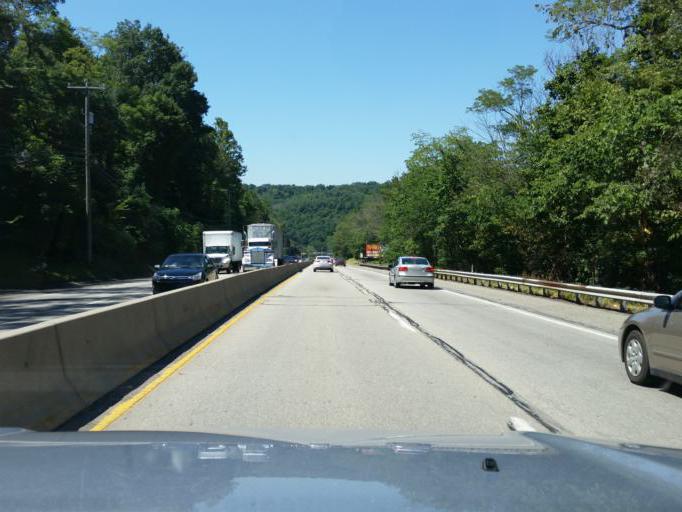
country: US
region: Pennsylvania
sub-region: Westmoreland County
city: Murrysville
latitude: 40.4297
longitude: -79.7150
